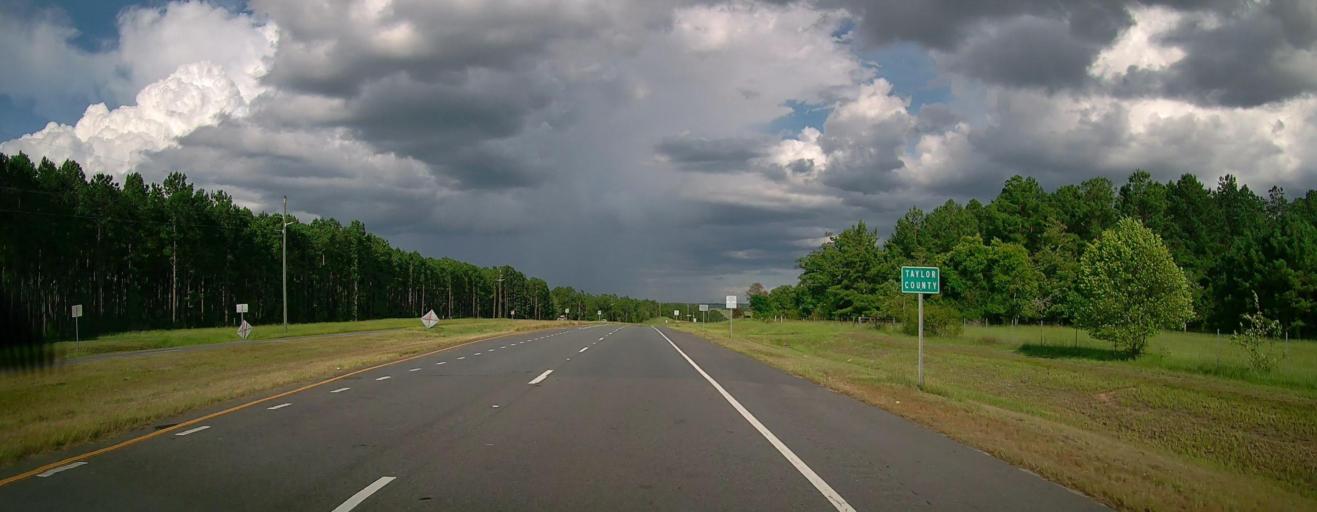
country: US
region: Georgia
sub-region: Talbot County
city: Talbotton
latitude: 32.5944
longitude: -84.4087
